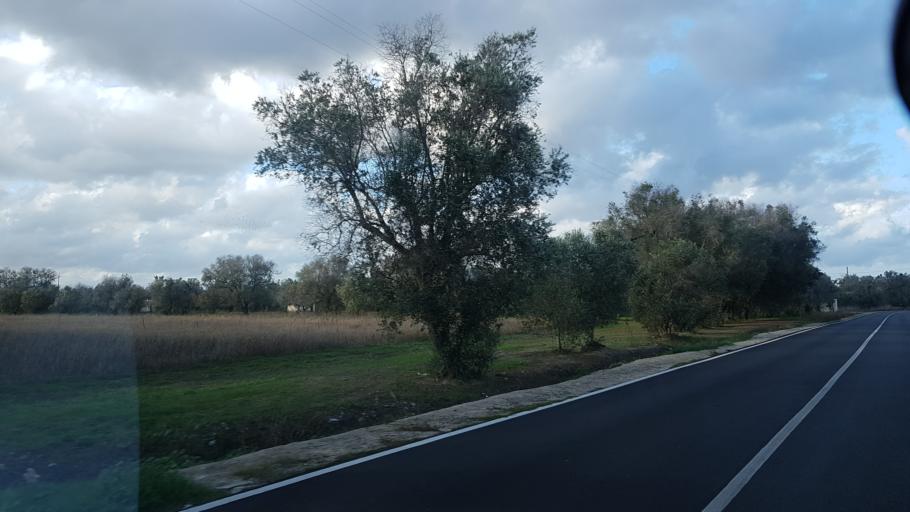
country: IT
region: Apulia
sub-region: Provincia di Brindisi
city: San Pietro Vernotico
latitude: 40.5057
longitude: 18.0080
